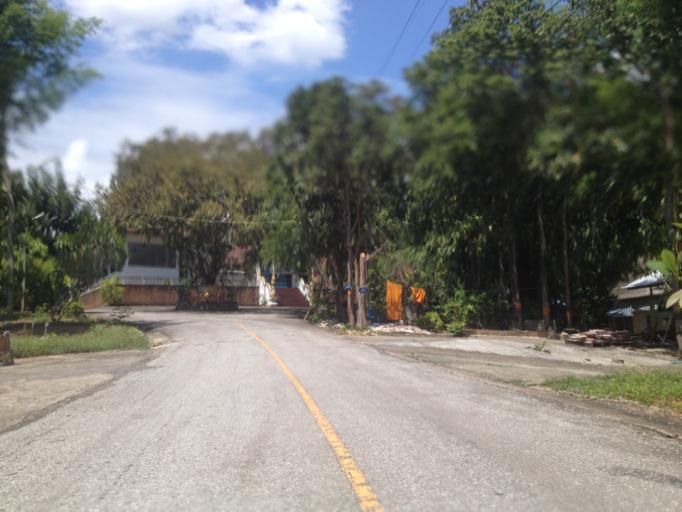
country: TH
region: Chiang Mai
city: Hang Dong
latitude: 18.7402
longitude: 98.9211
